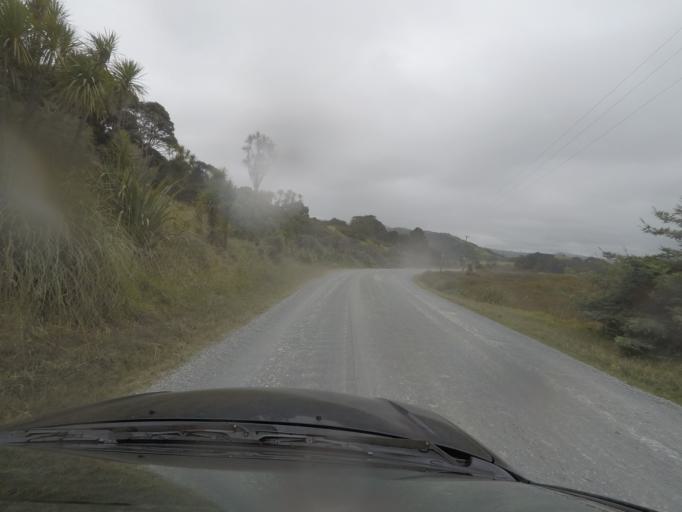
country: NZ
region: Auckland
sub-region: Auckland
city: Warkworth
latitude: -36.2487
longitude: 174.7196
